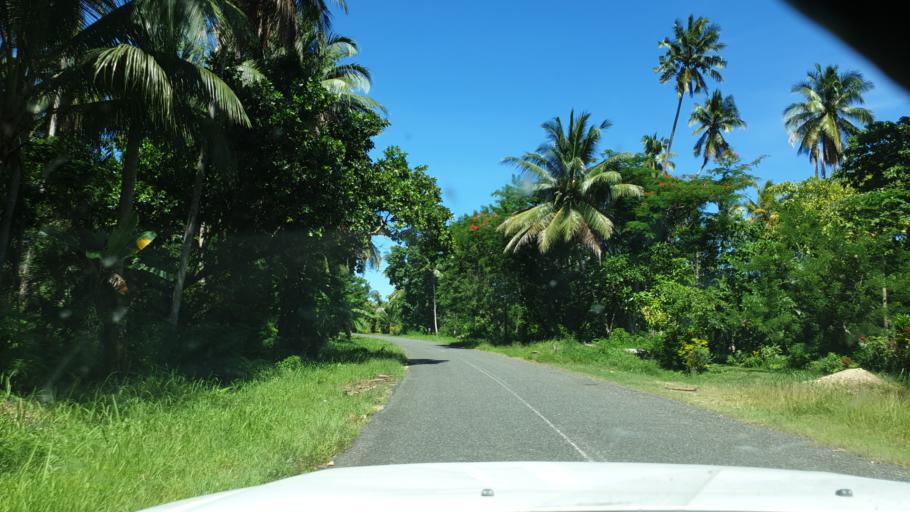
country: PG
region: Madang
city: Madang
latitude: -4.4640
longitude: 145.4116
